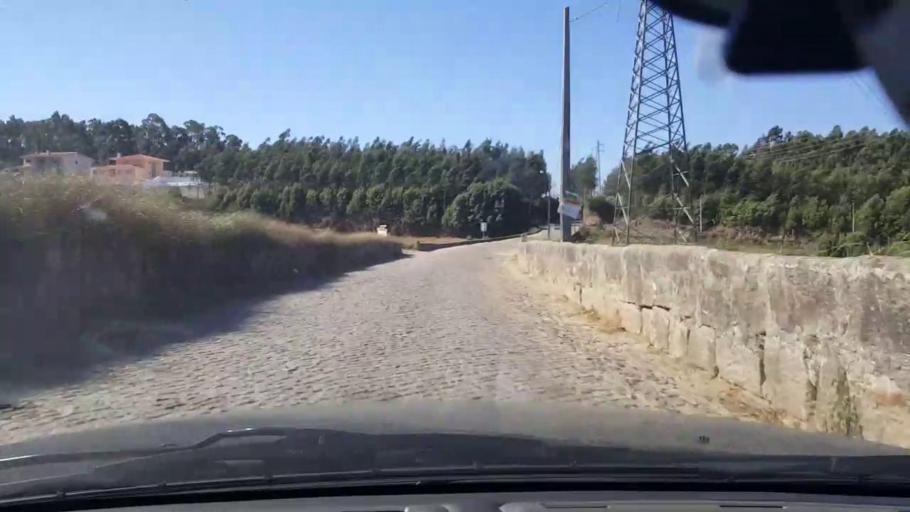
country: PT
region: Porto
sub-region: Maia
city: Gemunde
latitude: 41.2865
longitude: -8.6487
